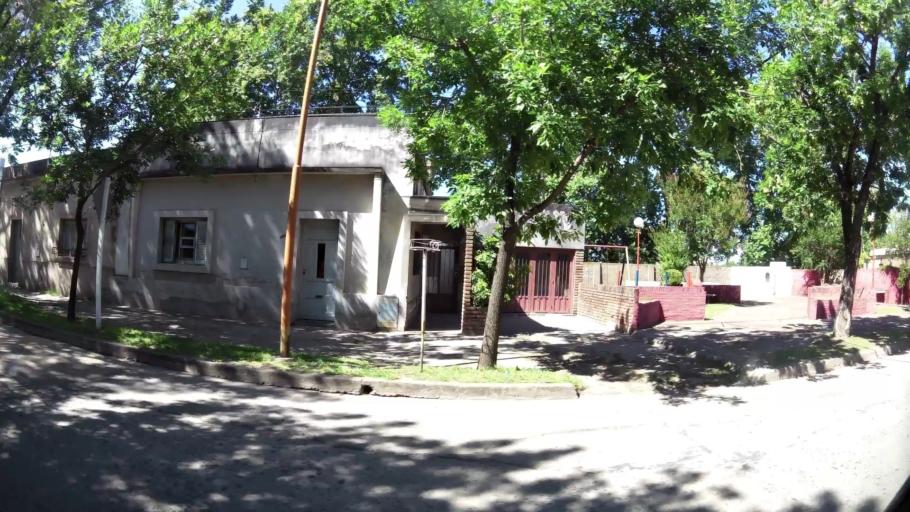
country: AR
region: Santa Fe
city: Esperanza
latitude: -31.4436
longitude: -60.9336
